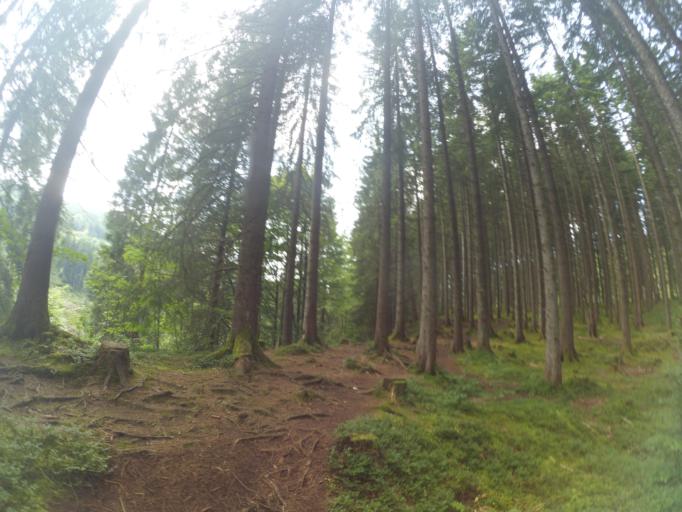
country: DE
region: Bavaria
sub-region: Swabia
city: Halblech
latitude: 47.5999
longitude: 10.8191
